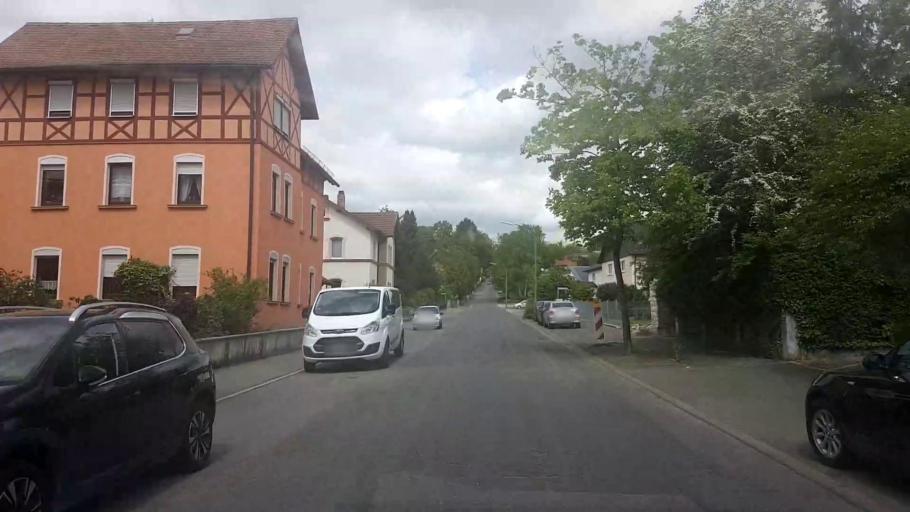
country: DE
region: Bavaria
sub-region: Upper Franconia
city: Lichtenfels
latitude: 50.1542
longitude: 11.0574
